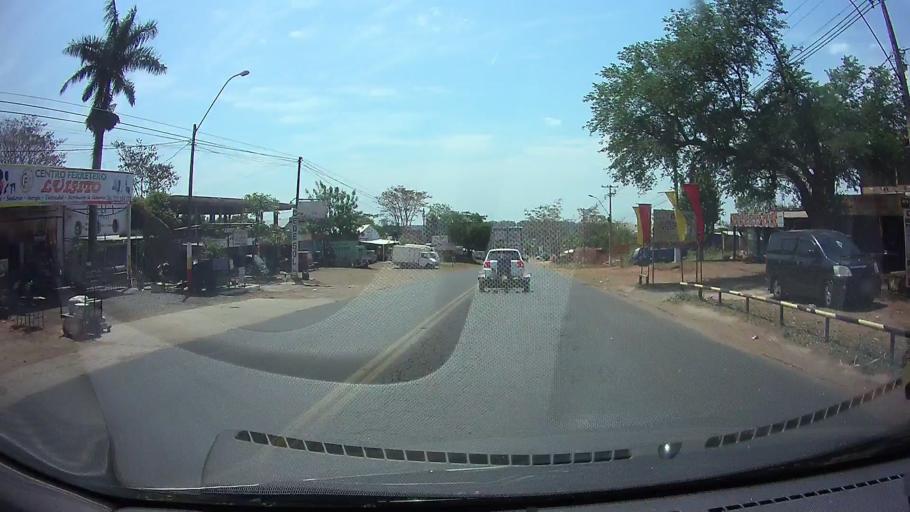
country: PY
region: Central
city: Capiata
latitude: -25.3986
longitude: -57.4655
